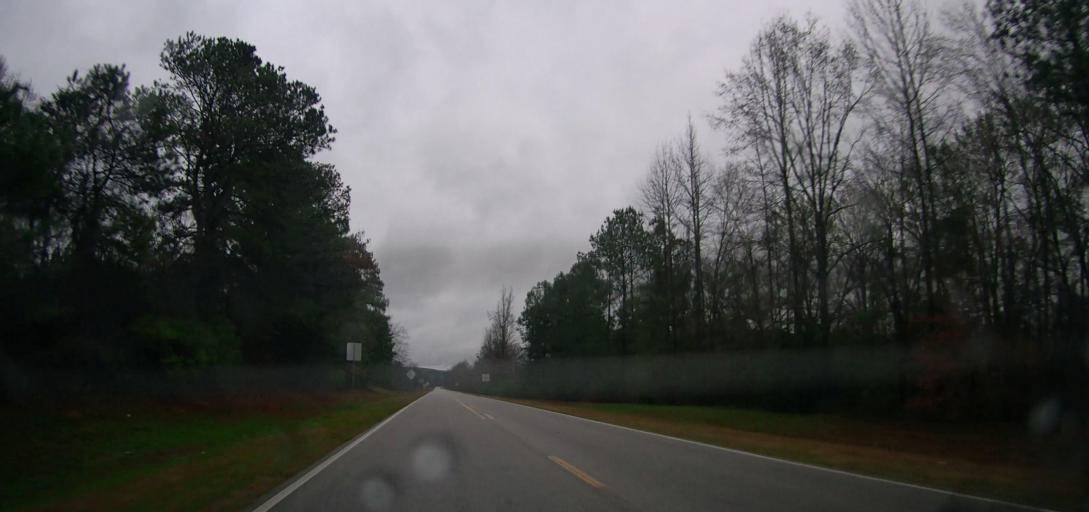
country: US
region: Alabama
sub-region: Bibb County
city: Centreville
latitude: 32.9270
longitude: -87.0468
